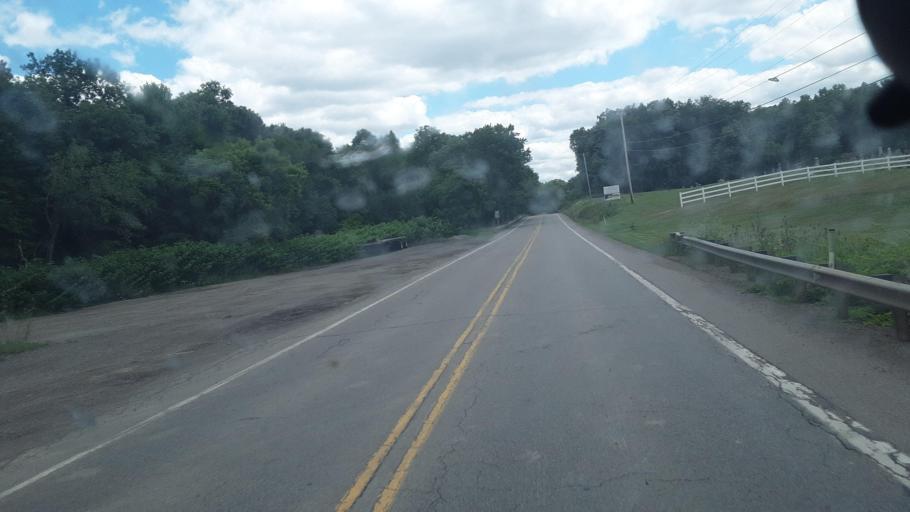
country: US
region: Pennsylvania
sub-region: Butler County
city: Slippery Rock
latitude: 41.0225
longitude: -80.1864
